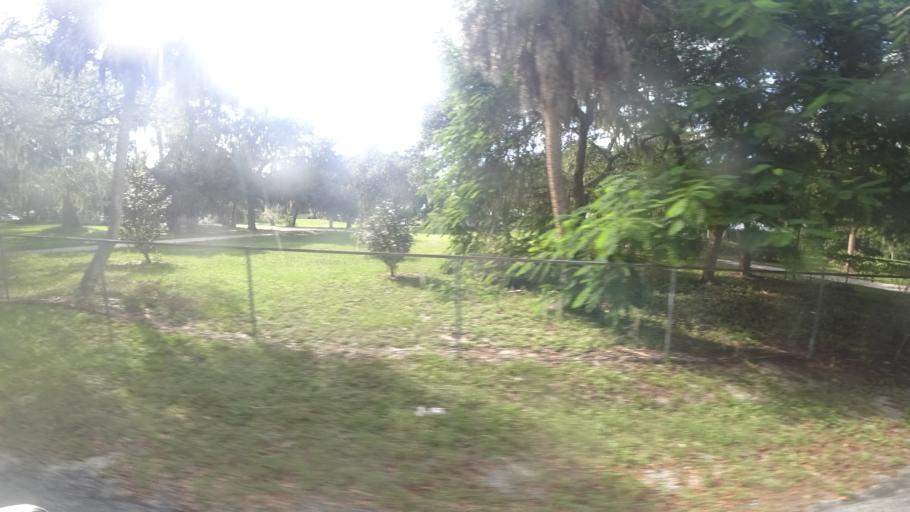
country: US
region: Florida
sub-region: Manatee County
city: Memphis
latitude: 27.6029
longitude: -82.5354
